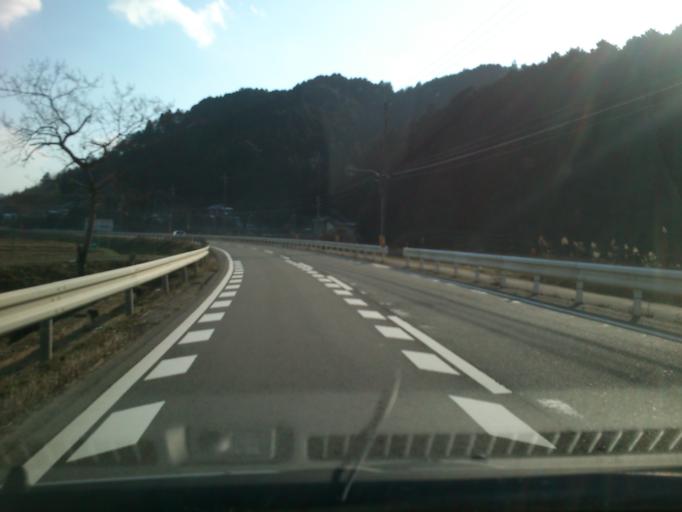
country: JP
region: Kyoto
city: Fukuchiyama
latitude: 35.4057
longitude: 135.1825
